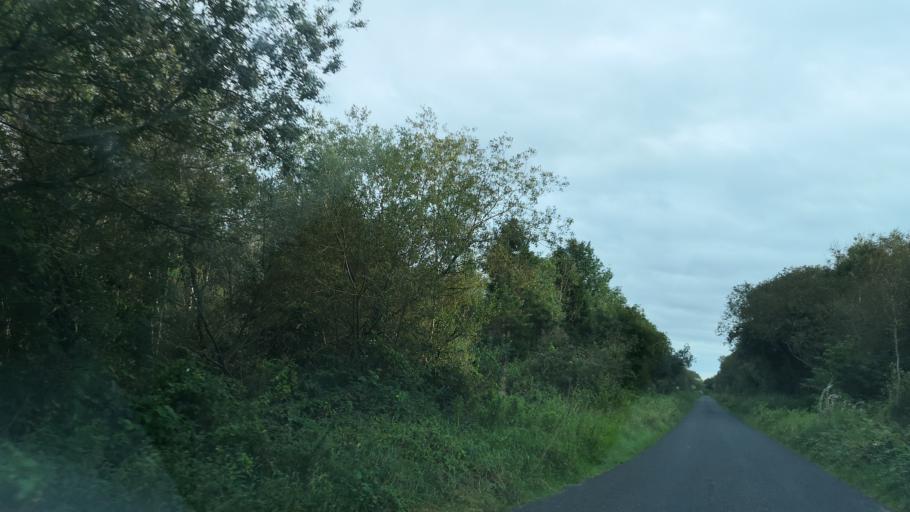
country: IE
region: Leinster
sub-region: Uibh Fhaili
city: Ferbane
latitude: 53.1955
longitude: -7.7257
